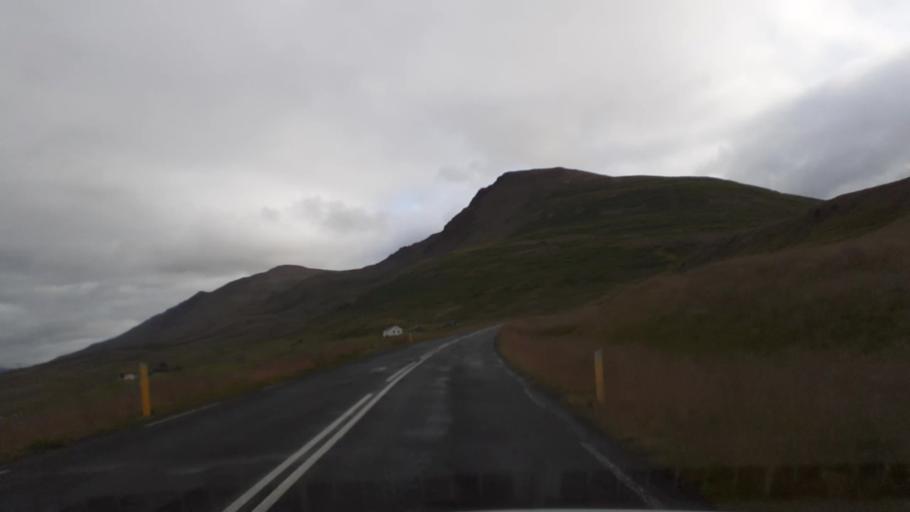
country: IS
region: Northeast
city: Akureyri
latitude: 65.8120
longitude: -18.0527
